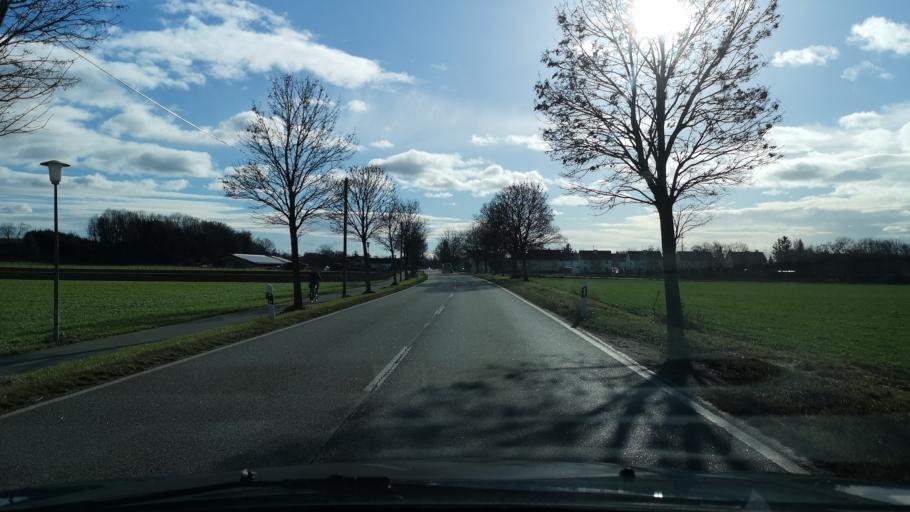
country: DE
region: Bavaria
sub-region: Upper Bavaria
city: Poing
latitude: 48.1615
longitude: 11.8153
